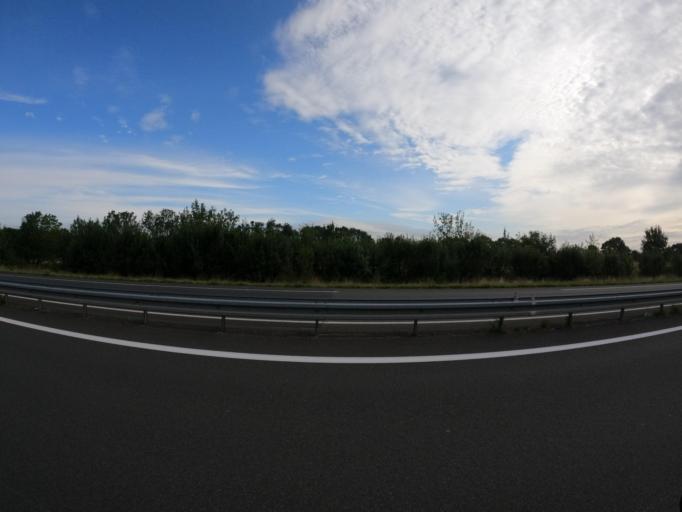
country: FR
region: Centre
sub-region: Departement d'Indre-et-Loire
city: Saint-Nicolas-de-Bourgueil
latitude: 47.2617
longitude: 0.1336
